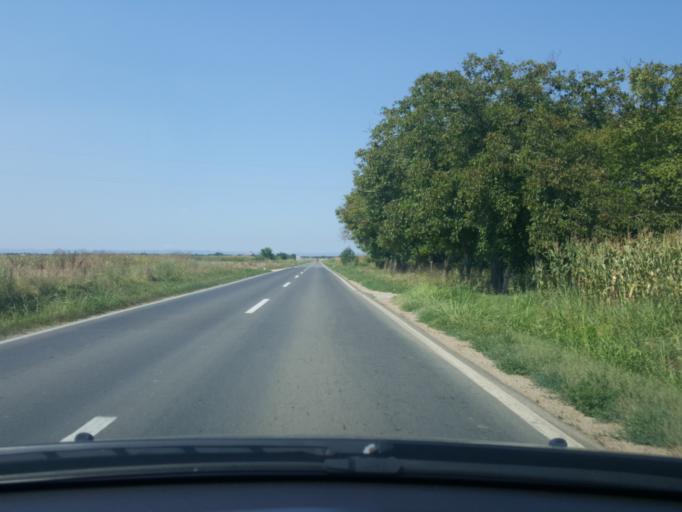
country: RS
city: Hrtkovci
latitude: 44.8553
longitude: 19.7712
